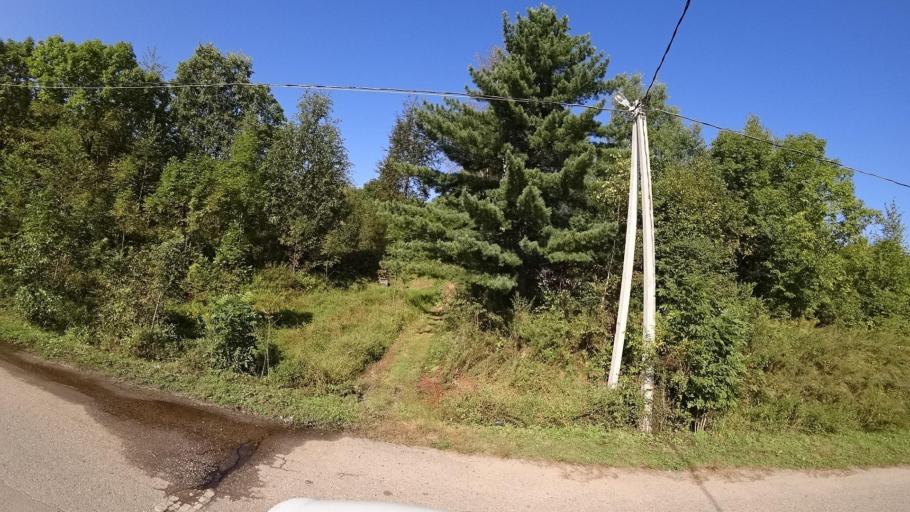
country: RU
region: Jewish Autonomous Oblast
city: Bira
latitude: 49.0098
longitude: 132.4732
